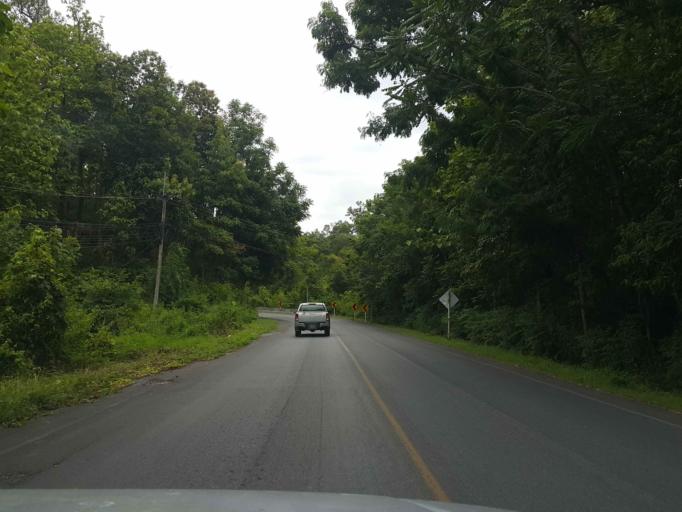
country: TH
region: Lampang
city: Thoen
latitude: 17.6160
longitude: 99.3212
